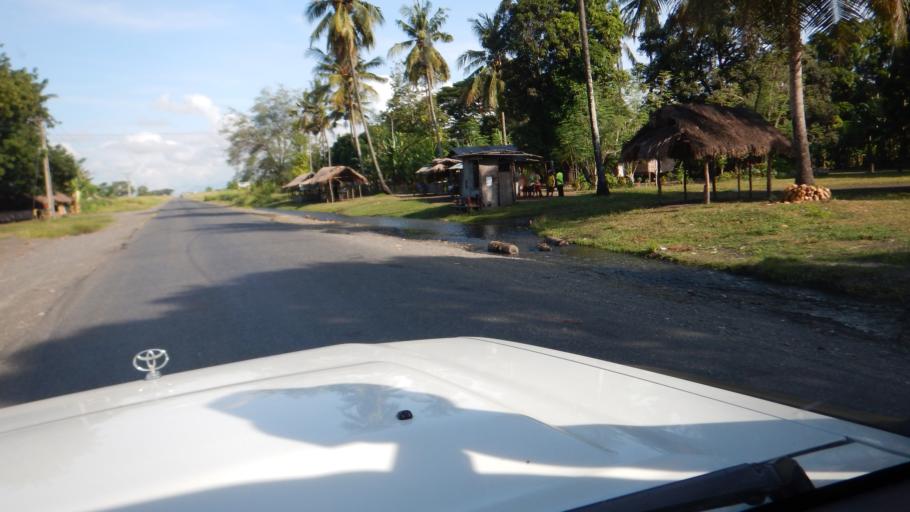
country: PG
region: Morobe
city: Lae
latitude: -6.5117
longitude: 146.4702
